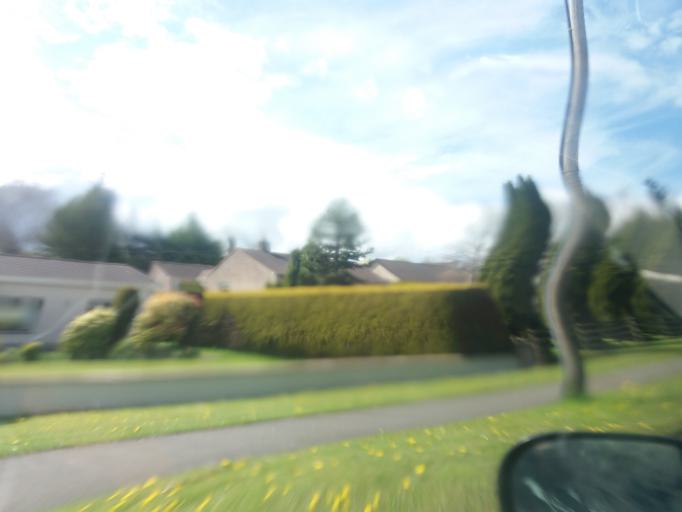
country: GB
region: Northern Ireland
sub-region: Fermanagh District
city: Enniskillen
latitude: 54.3582
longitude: -7.6712
